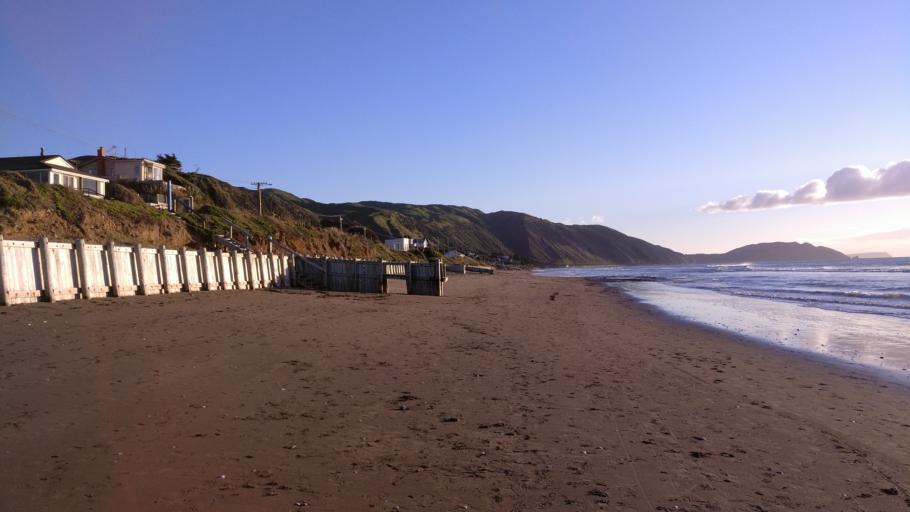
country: NZ
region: Wellington
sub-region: Kapiti Coast District
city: Paraparaumu
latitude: -40.9770
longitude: 174.9568
